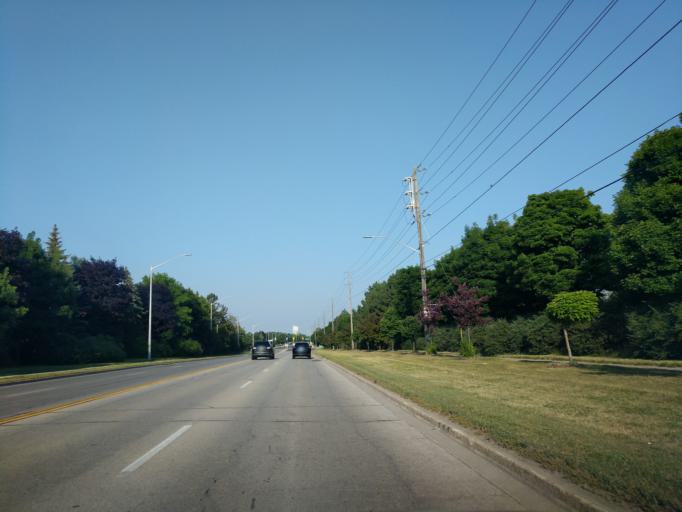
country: CA
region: Ontario
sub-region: York
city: Richmond Hill
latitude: 43.8597
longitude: -79.3993
